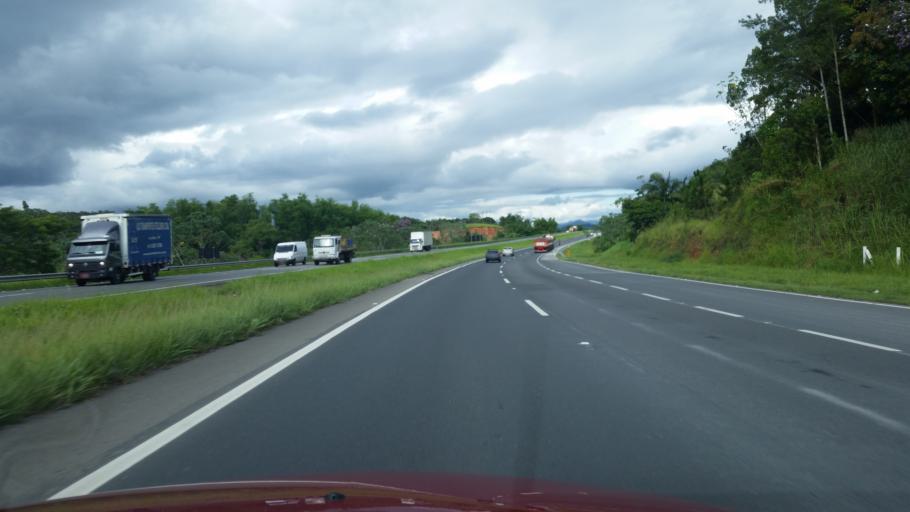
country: BR
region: Sao Paulo
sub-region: Miracatu
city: Miracatu
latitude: -24.2938
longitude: -47.4778
